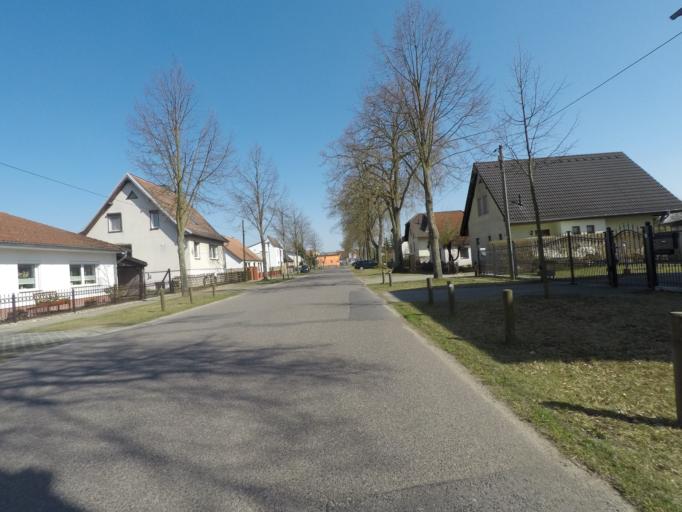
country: DE
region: Brandenburg
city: Marienwerder
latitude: 52.8533
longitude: 13.6794
